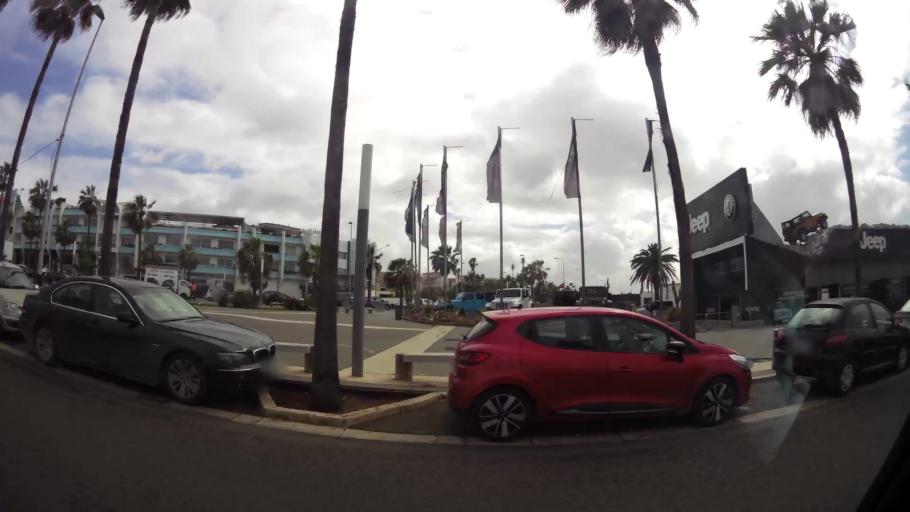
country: MA
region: Grand Casablanca
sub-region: Casablanca
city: Casablanca
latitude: 33.5959
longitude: -7.6689
